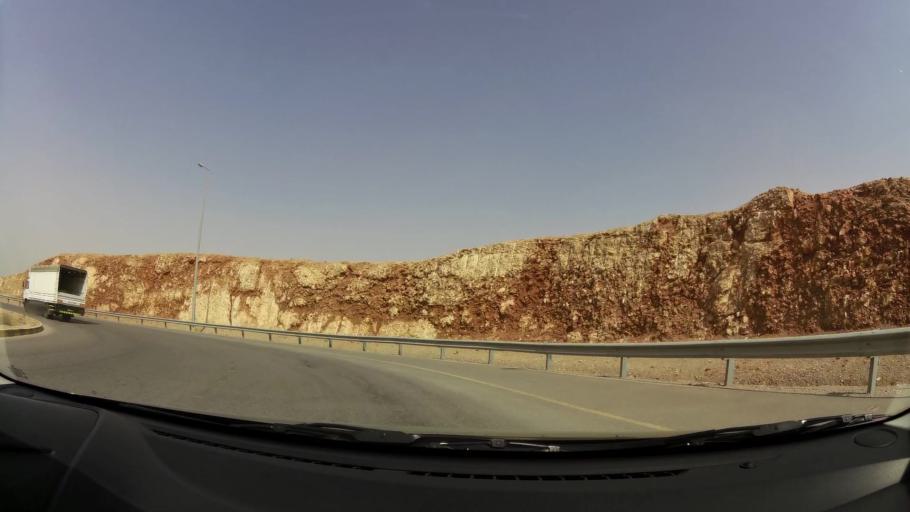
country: OM
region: Muhafazat Masqat
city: Bawshar
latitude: 23.5539
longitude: 58.3381
